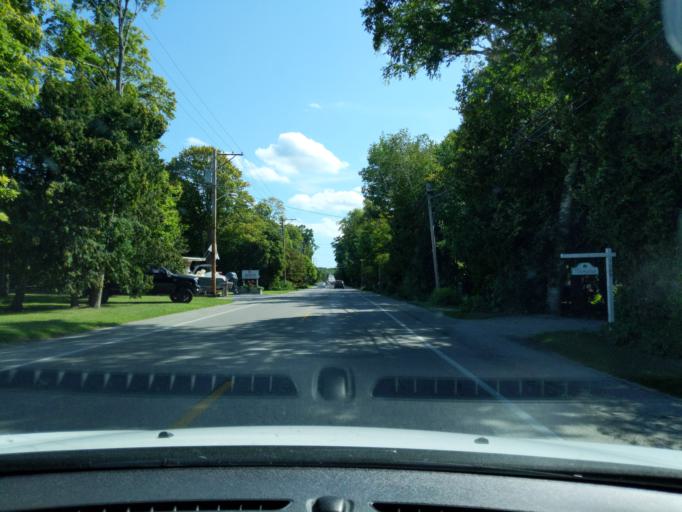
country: US
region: Wisconsin
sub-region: Door County
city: Sturgeon Bay
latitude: 45.1999
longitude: -87.1189
